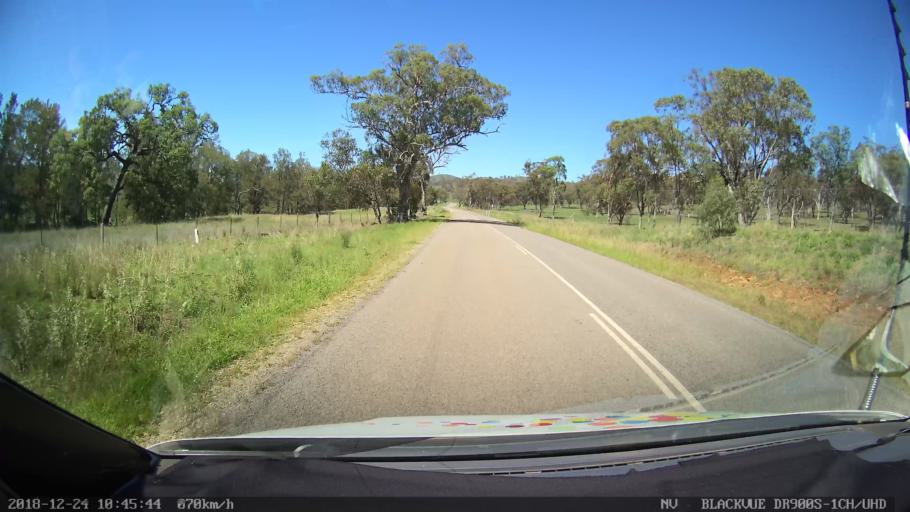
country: AU
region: New South Wales
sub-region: Upper Hunter Shire
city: Merriwa
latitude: -31.9055
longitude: 150.4336
